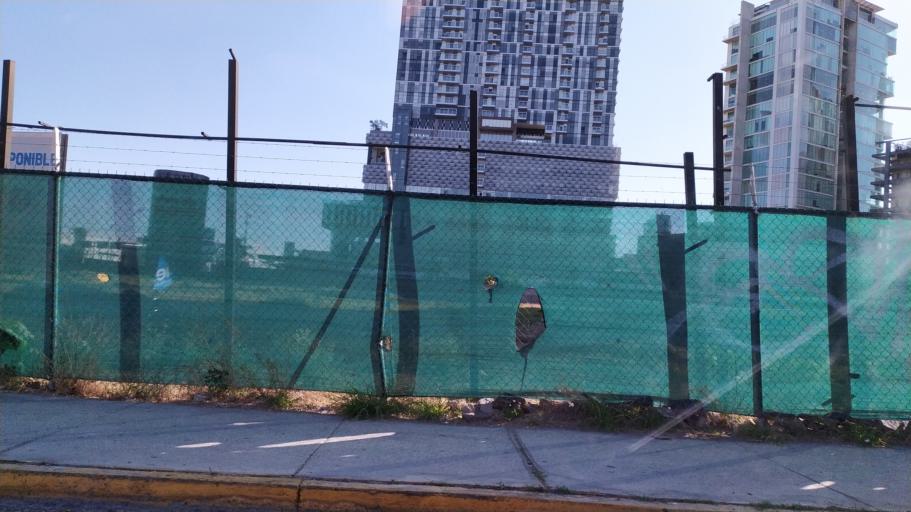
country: MX
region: Jalisco
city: Zapopan2
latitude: 20.7108
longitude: -103.4079
